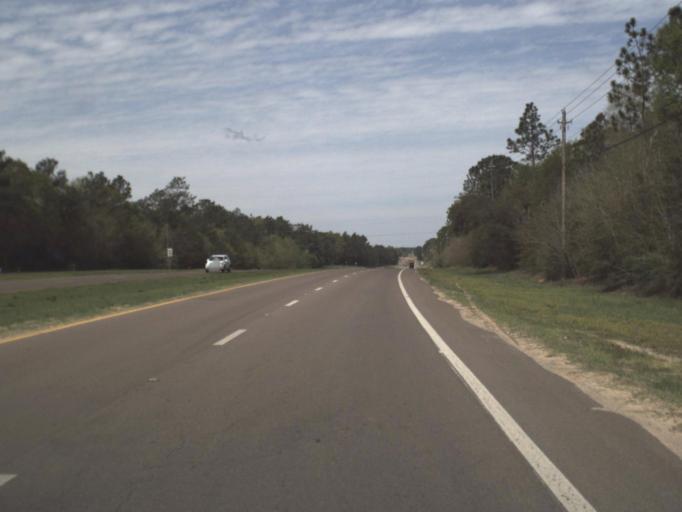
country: US
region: Florida
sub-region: Okaloosa County
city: Crestview
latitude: 30.7559
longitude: -86.5285
